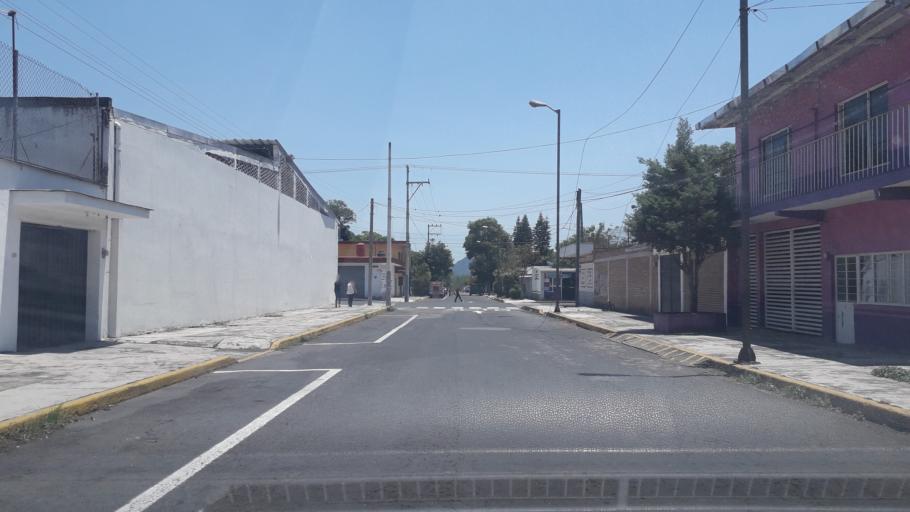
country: MX
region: Veracruz
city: Jalapilla
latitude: 18.8381
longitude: -97.0913
